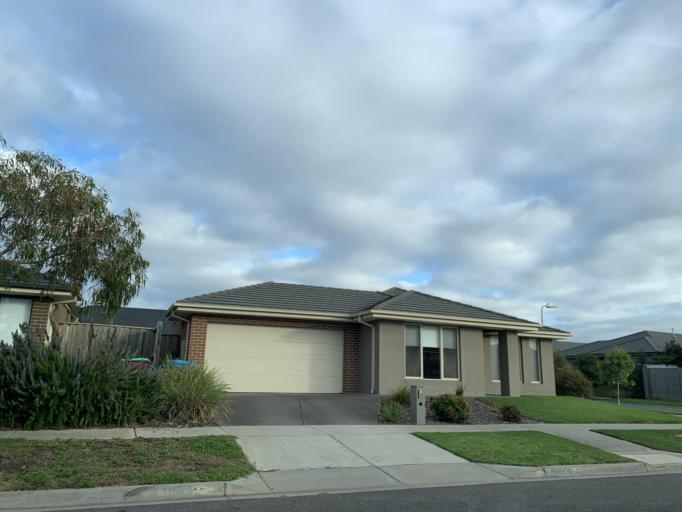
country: AU
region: Victoria
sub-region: Casey
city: Cranbourne East
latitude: -38.1252
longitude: 145.2936
